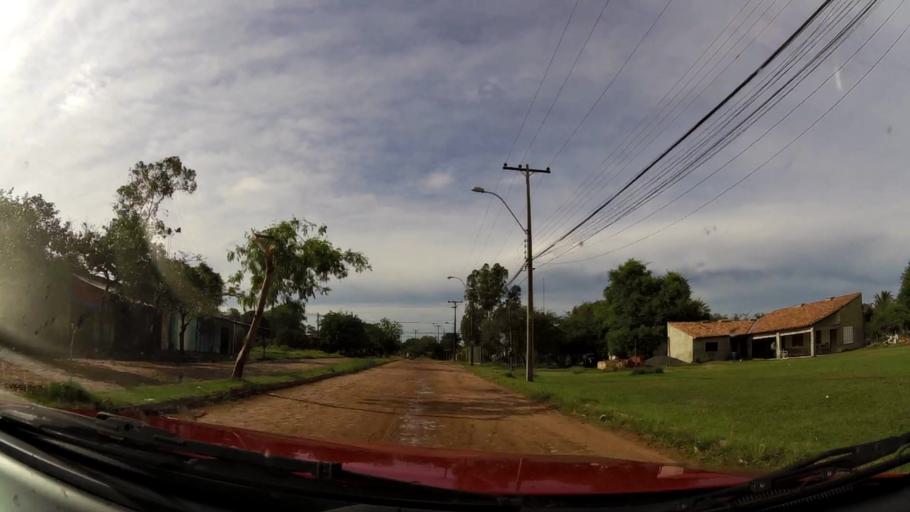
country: PY
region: Central
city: Limpio
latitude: -25.1692
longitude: -57.4894
